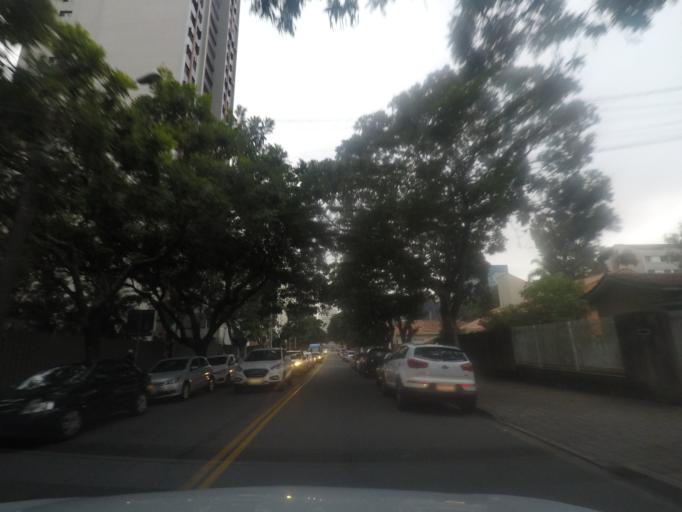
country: BR
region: Parana
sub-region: Curitiba
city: Curitiba
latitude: -25.4338
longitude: -49.2518
